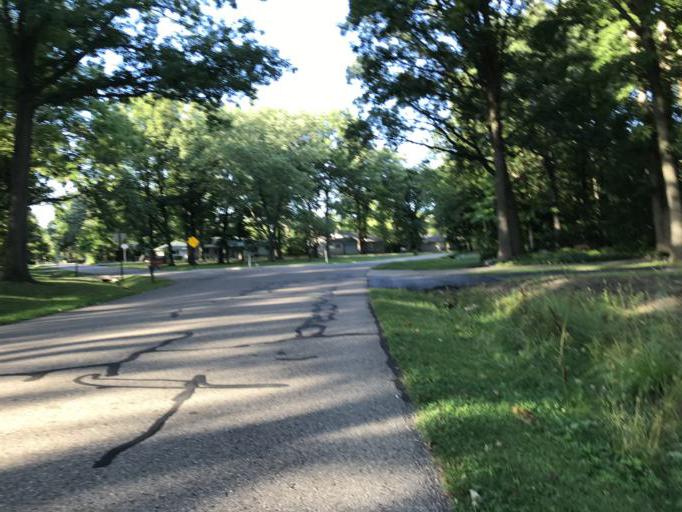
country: US
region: Michigan
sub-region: Oakland County
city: Farmington Hills
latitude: 42.4780
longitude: -83.3511
